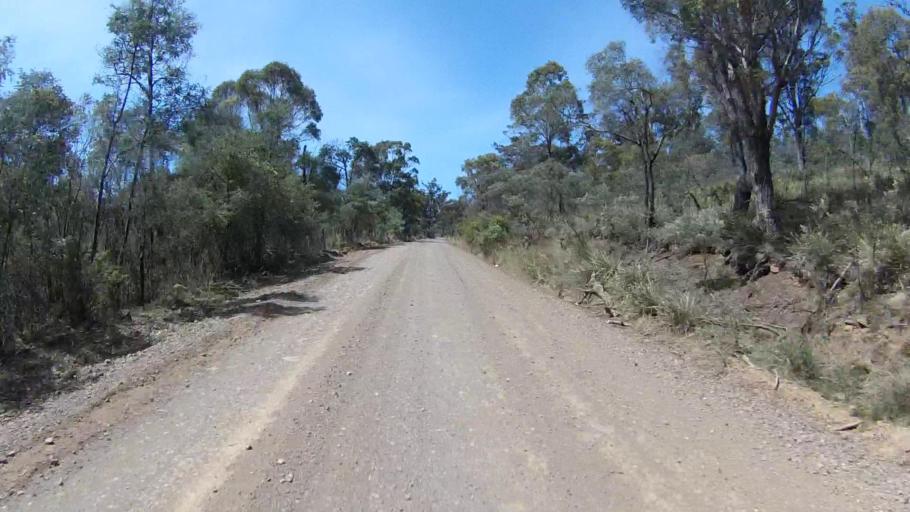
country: AU
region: Tasmania
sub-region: Sorell
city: Sorell
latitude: -42.6464
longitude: 147.7422
